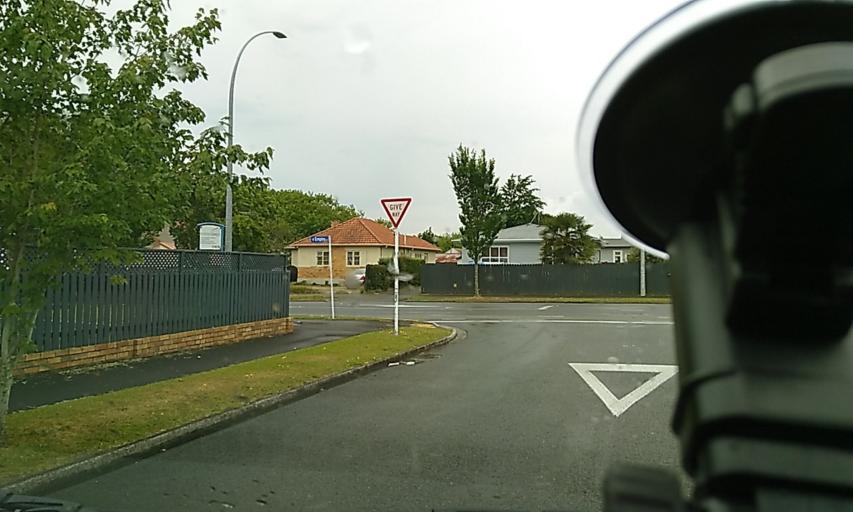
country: NZ
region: Waikato
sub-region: Hamilton City
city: Hamilton
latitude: -37.7841
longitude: 175.2628
